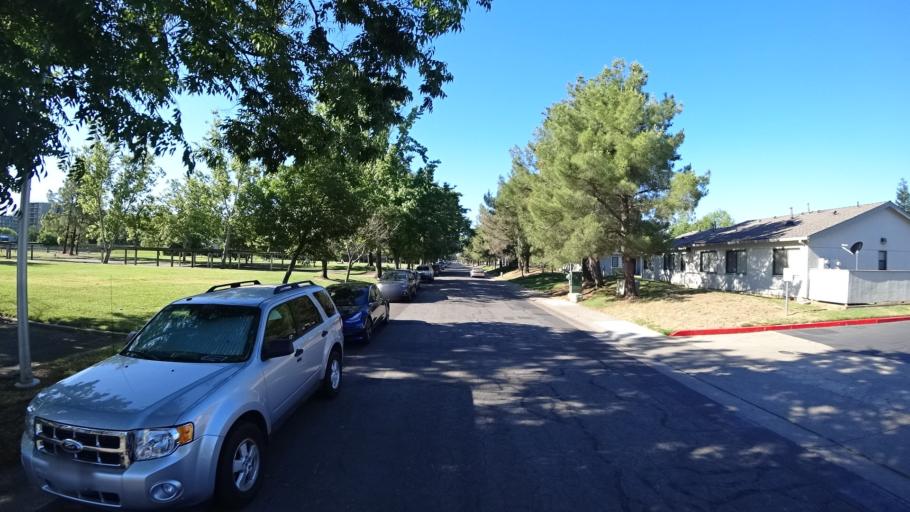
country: US
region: California
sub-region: Sacramento County
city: Parkway
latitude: 38.5498
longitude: -121.4441
